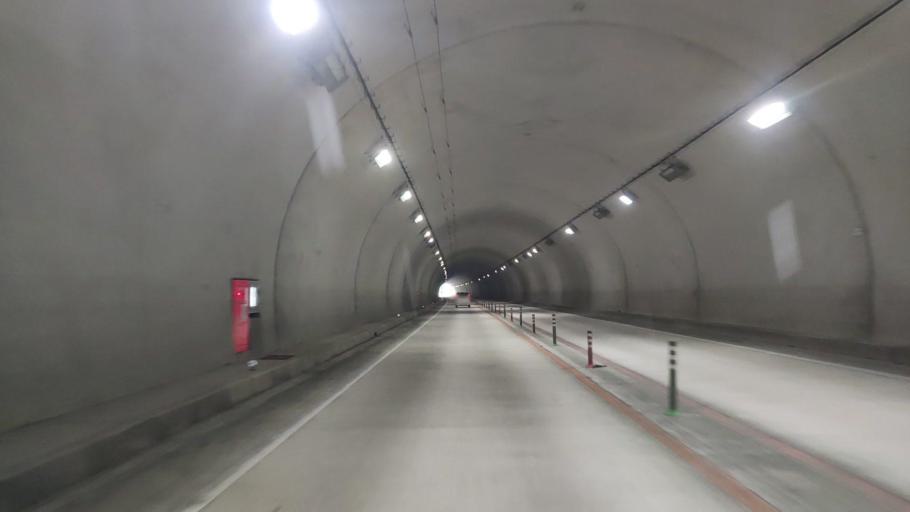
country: JP
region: Wakayama
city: Shingu
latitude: 33.6166
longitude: 135.9173
